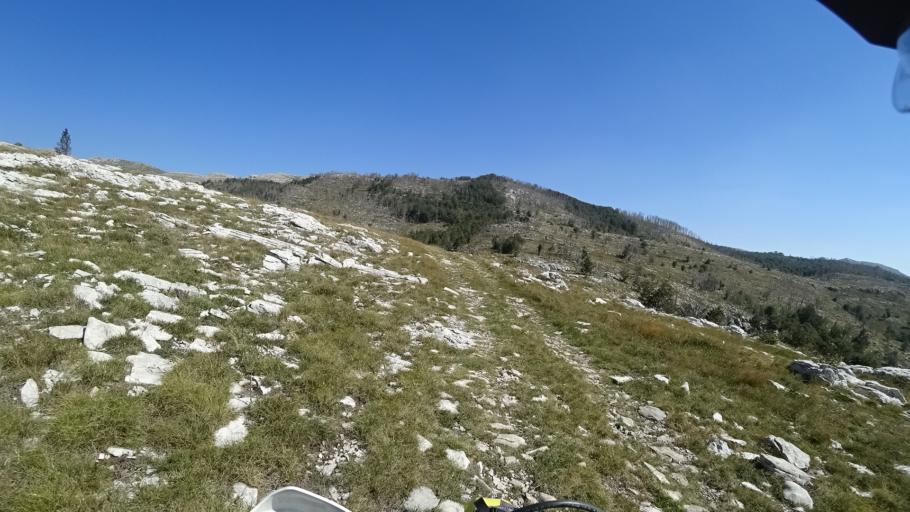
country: HR
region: Splitsko-Dalmatinska
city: Hrvace
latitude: 43.9130
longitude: 16.6089
